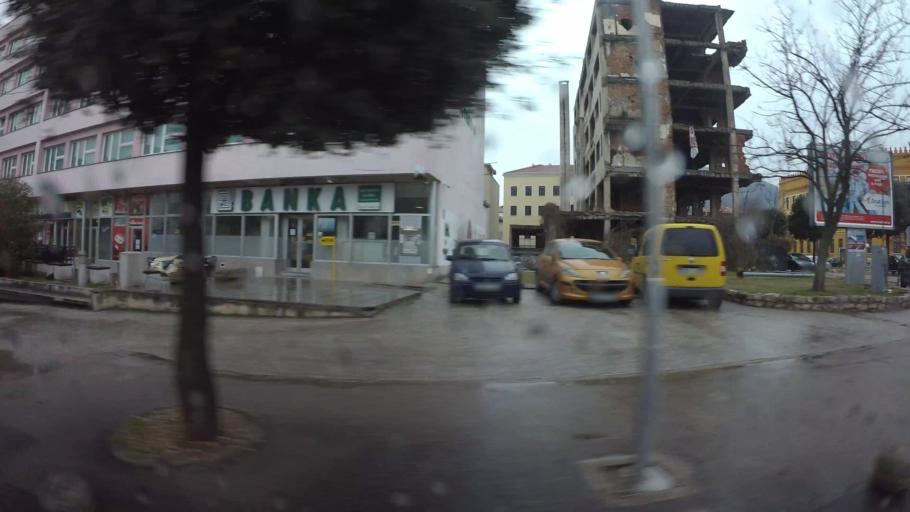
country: BA
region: Federation of Bosnia and Herzegovina
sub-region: Hercegovacko-Bosanski Kanton
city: Mostar
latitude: 43.3436
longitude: 17.8080
